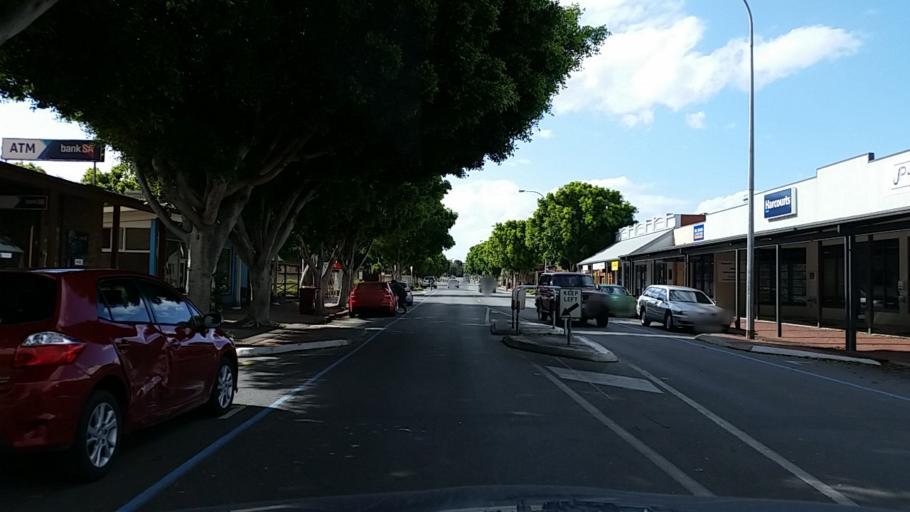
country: AU
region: South Australia
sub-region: Alexandrina
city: Goolwa
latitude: -35.5015
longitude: 138.7825
